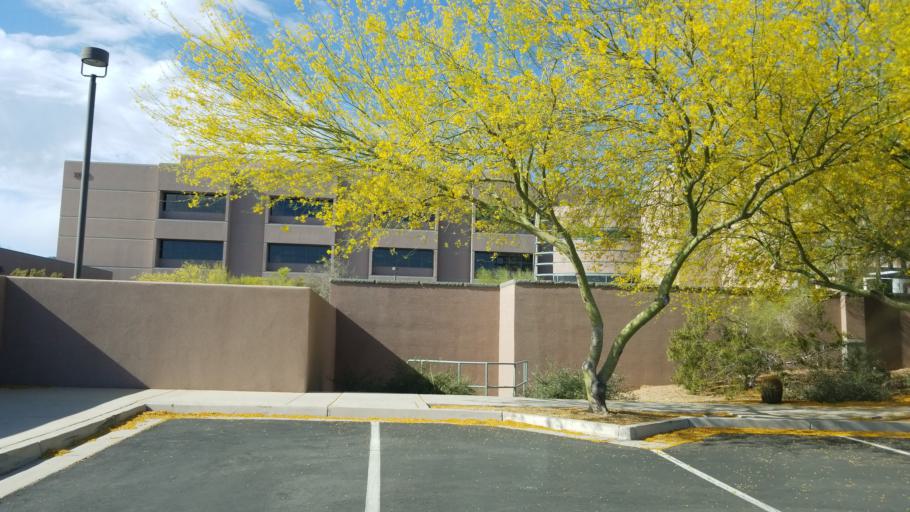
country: US
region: Arizona
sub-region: Maricopa County
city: Fountain Hills
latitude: 33.5832
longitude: -111.7950
